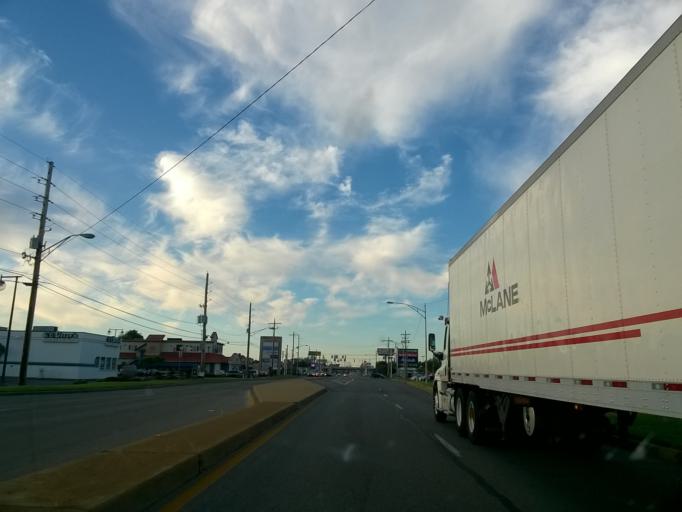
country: US
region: Indiana
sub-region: Vanderburgh County
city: Melody Hill
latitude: 37.9826
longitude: -87.4928
